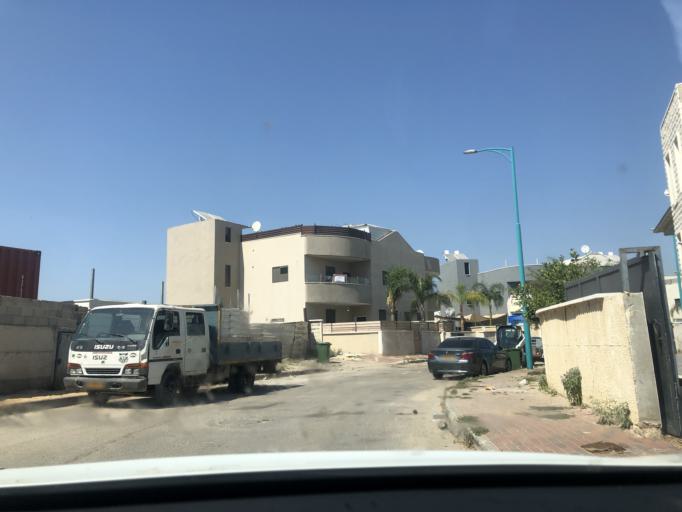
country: IL
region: Central District
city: Lod
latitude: 31.9540
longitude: 34.8747
